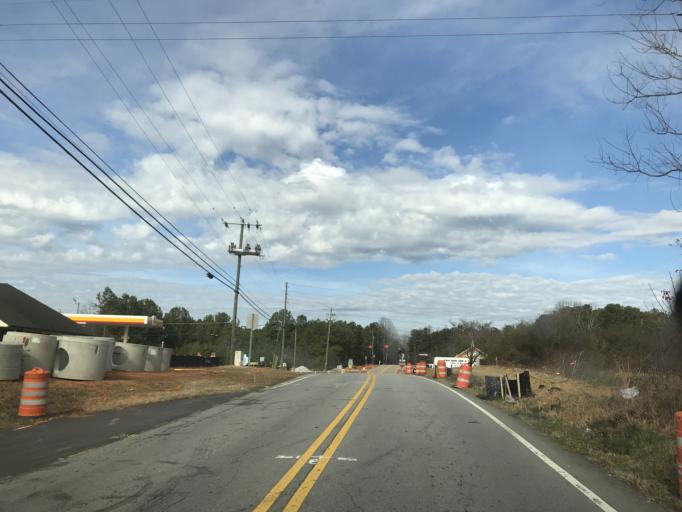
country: US
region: Georgia
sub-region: Carroll County
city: Villa Rica
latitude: 33.8036
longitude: -84.8407
